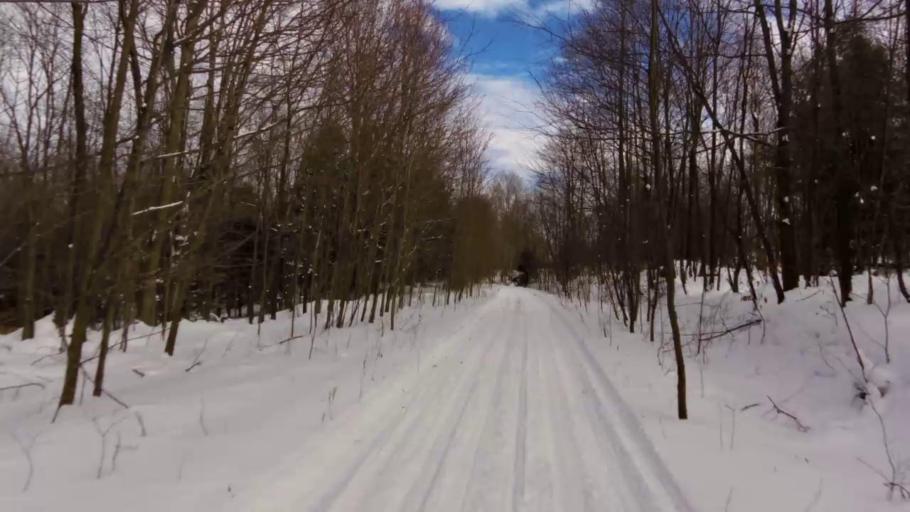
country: US
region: Pennsylvania
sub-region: McKean County
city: Foster Brook
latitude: 42.0106
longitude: -78.5623
